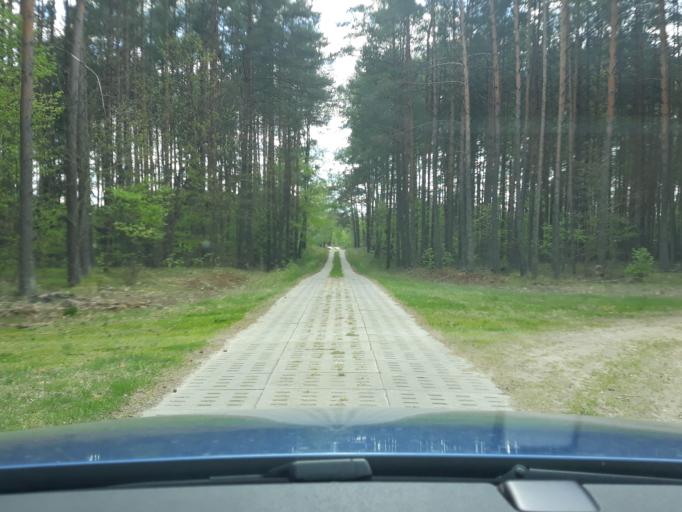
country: PL
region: Pomeranian Voivodeship
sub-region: Powiat czluchowski
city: Przechlewo
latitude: 53.7490
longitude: 17.3130
